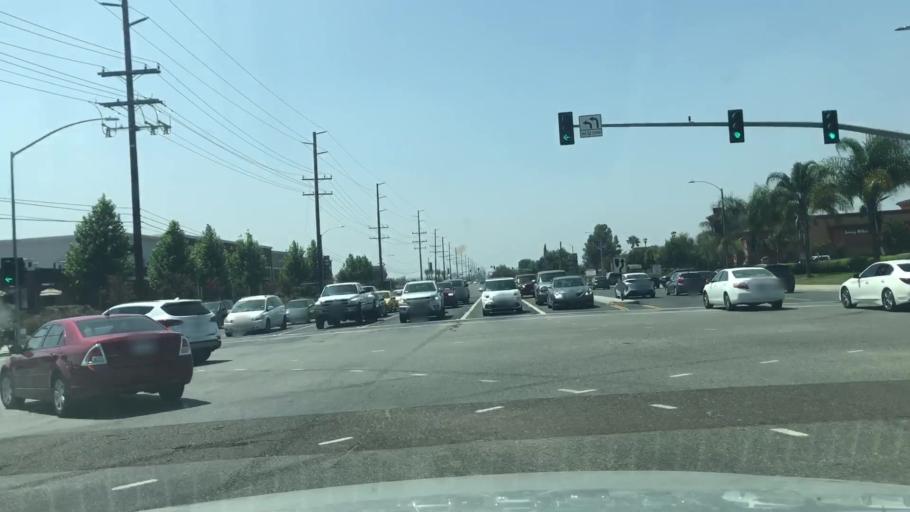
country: US
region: California
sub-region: Riverside County
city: Sun City
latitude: 33.6850
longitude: -117.1754
